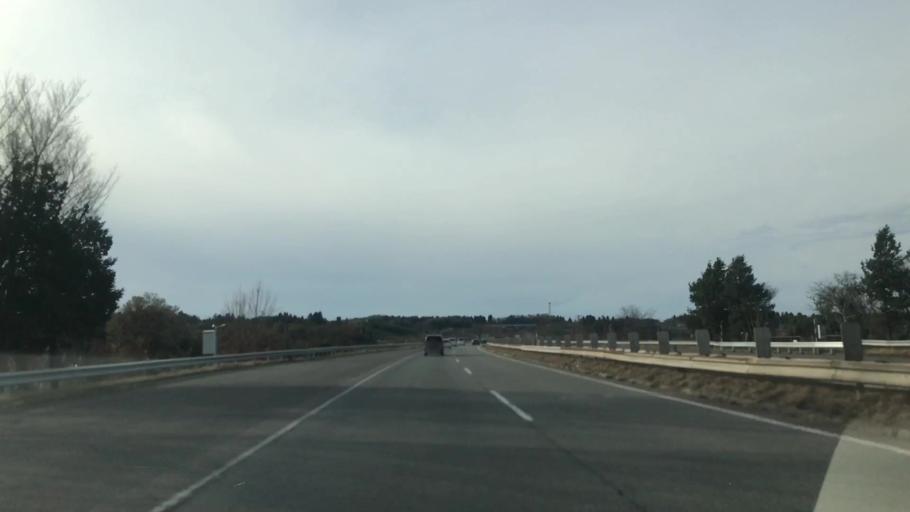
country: JP
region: Toyama
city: Kuragaki-kosugi
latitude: 36.6797
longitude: 137.1255
